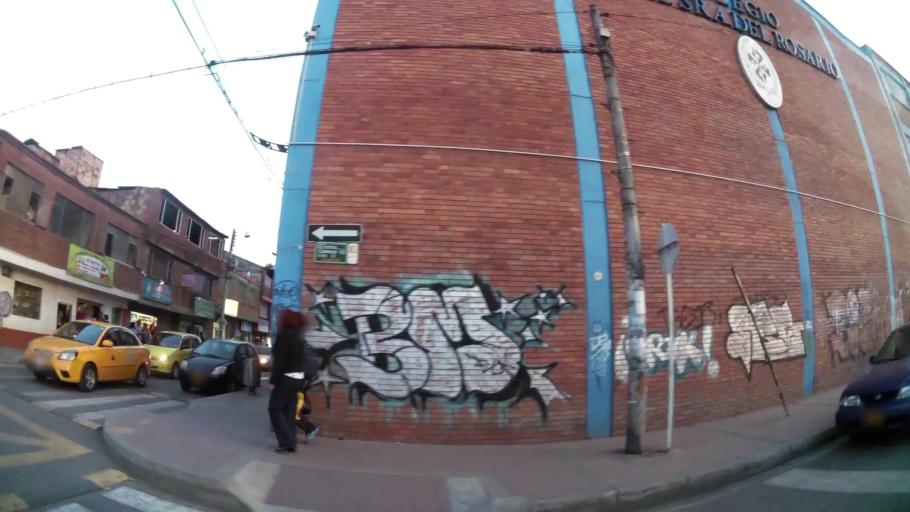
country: CO
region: Cundinamarca
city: Funza
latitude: 4.7150
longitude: -74.2123
